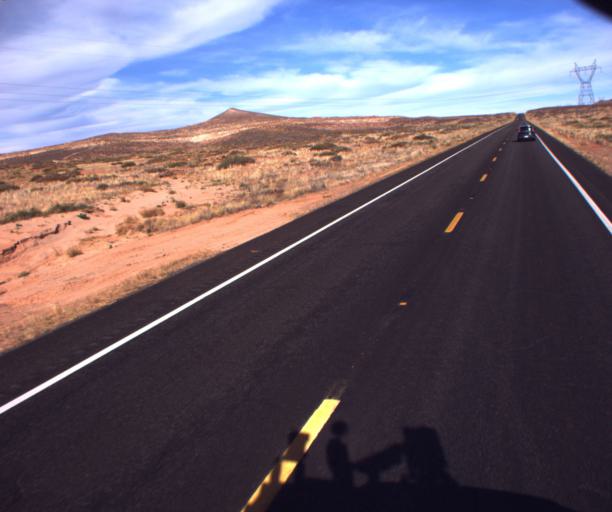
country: US
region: Arizona
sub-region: Apache County
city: Many Farms
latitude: 36.9429
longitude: -109.5395
